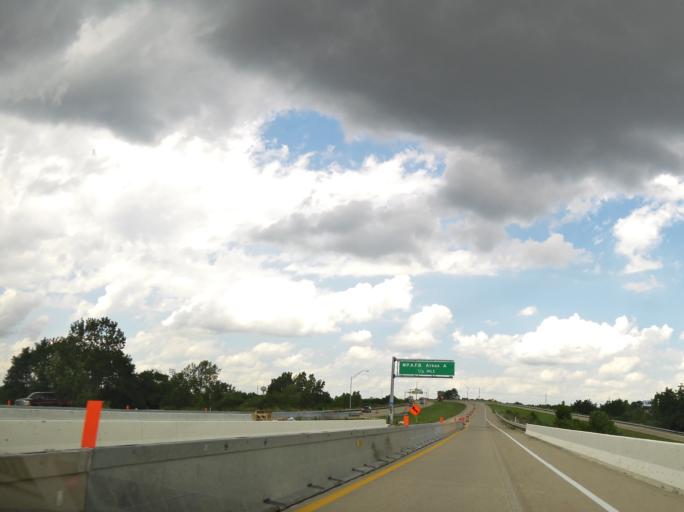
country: US
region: Ohio
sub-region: Greene County
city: Wright-Patterson AFB
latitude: 39.7880
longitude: -84.0453
